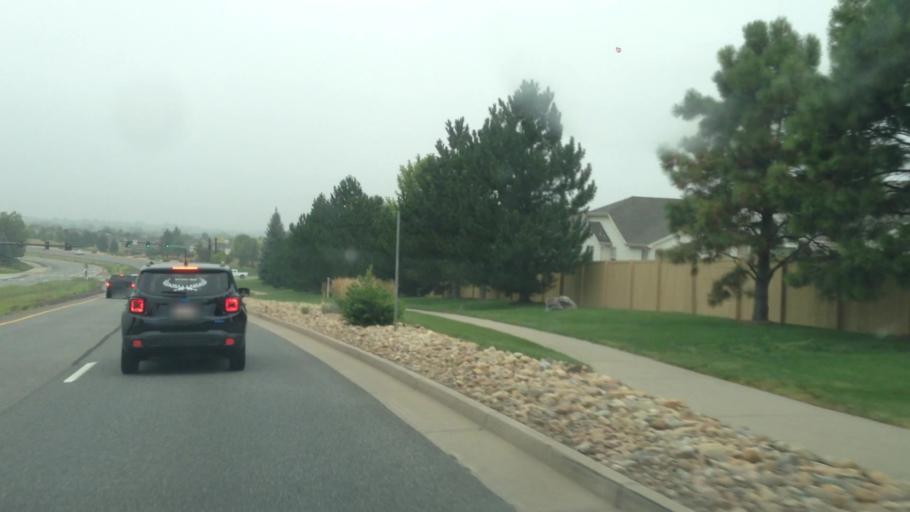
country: US
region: Colorado
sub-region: Douglas County
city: Parker
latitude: 39.6045
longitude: -104.7279
